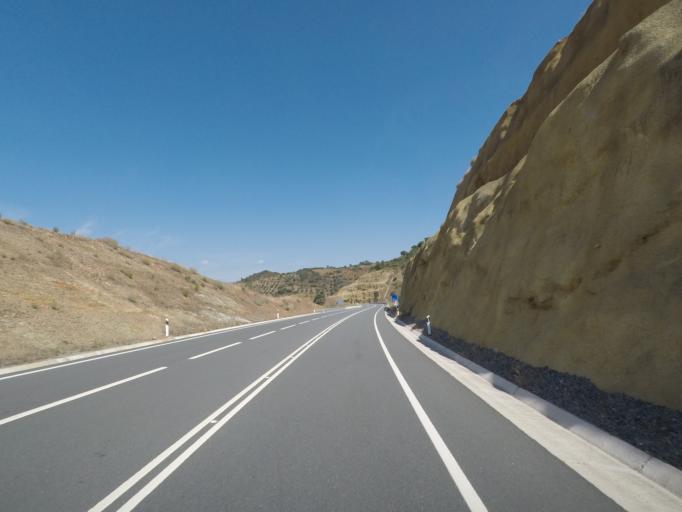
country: PT
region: Braganca
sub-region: Alfandega da Fe
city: Alfandega da Fe
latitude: 41.2990
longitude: -6.8999
